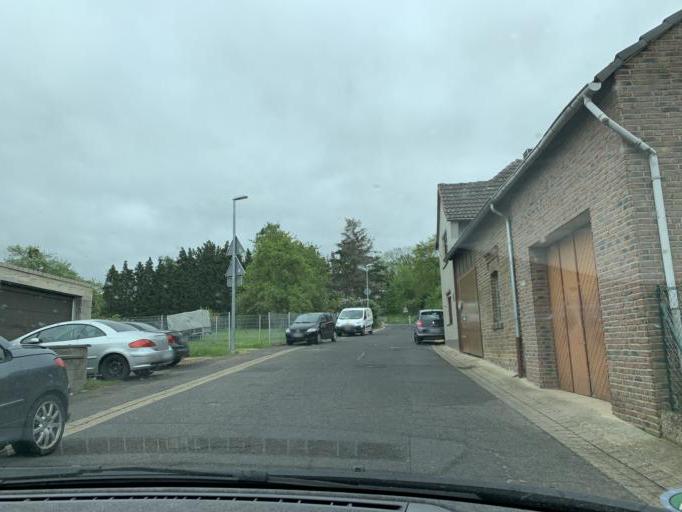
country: DE
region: North Rhine-Westphalia
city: Zulpich
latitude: 50.6645
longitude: 6.6716
